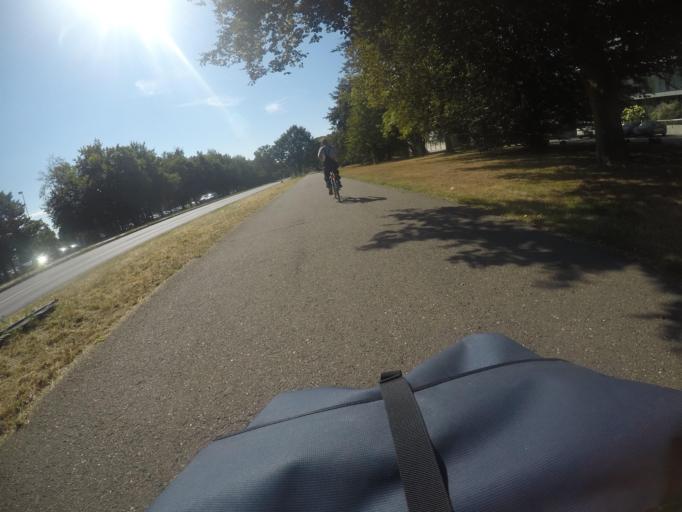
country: DE
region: North Rhine-Westphalia
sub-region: Regierungsbezirk Koln
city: Leverkusen
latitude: 51.0043
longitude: 6.9949
